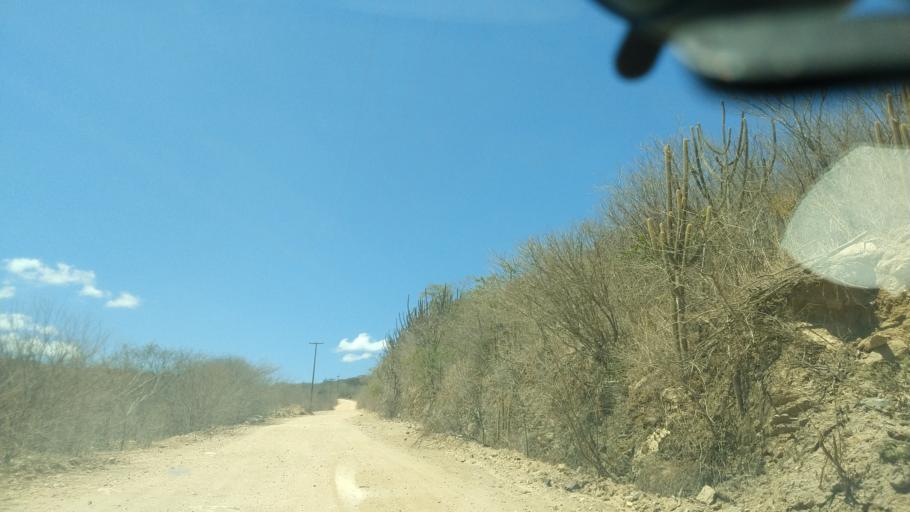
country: BR
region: Rio Grande do Norte
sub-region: Cerro Cora
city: Cerro Cora
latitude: -6.0108
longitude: -36.3195
